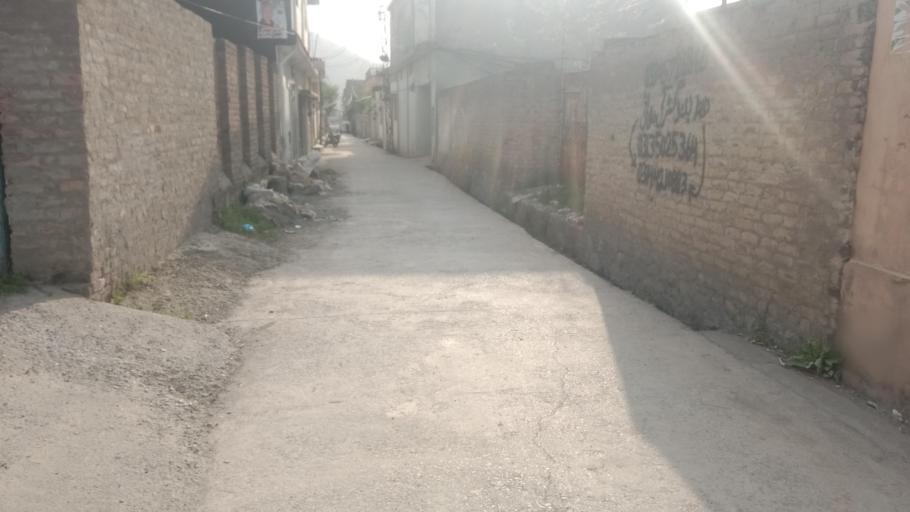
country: PK
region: Khyber Pakhtunkhwa
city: Abbottabad
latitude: 34.1601
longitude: 73.2619
